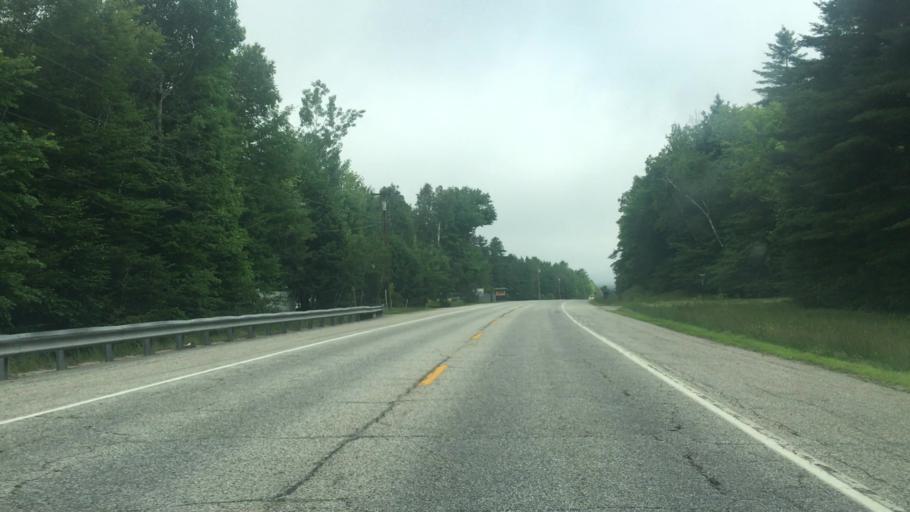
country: US
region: Maine
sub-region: Oxford County
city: Paris
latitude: 44.2630
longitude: -70.5151
